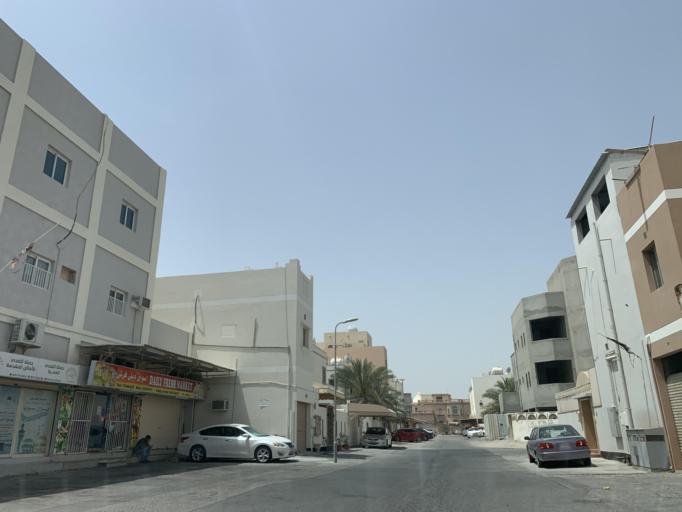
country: BH
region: Northern
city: Madinat `Isa
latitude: 26.1622
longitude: 50.5277
